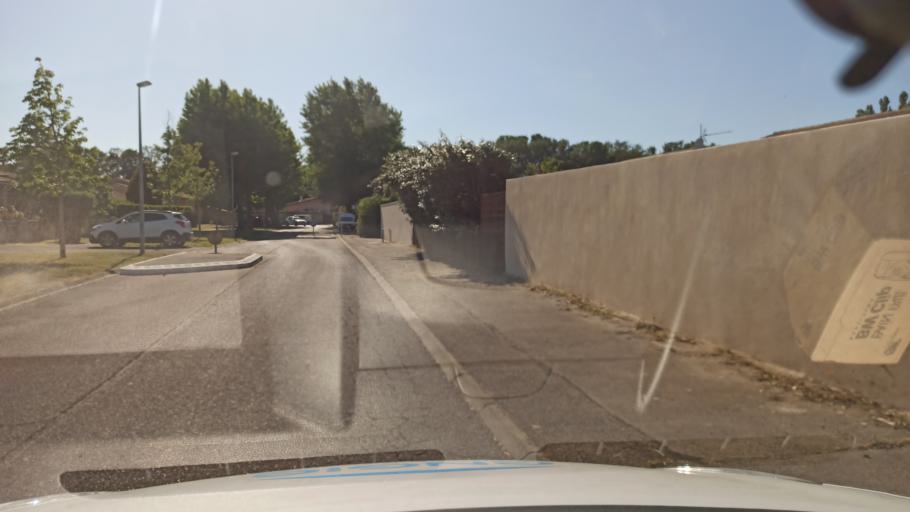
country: FR
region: Provence-Alpes-Cote d'Azur
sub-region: Departement du Vaucluse
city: Morieres-les-Avignon
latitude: 43.9570
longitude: 4.8860
